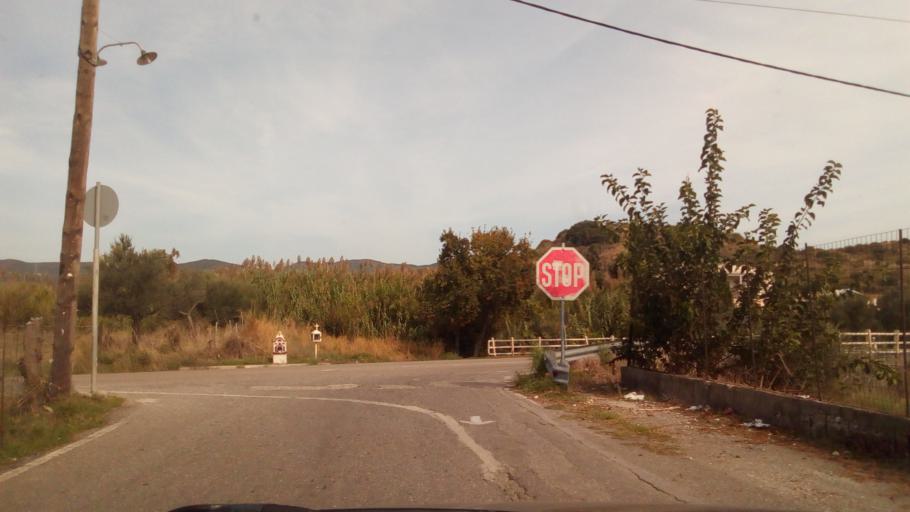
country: GR
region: West Greece
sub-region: Nomos Aitolias kai Akarnanias
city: Antirrio
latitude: 38.3421
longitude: 21.7671
